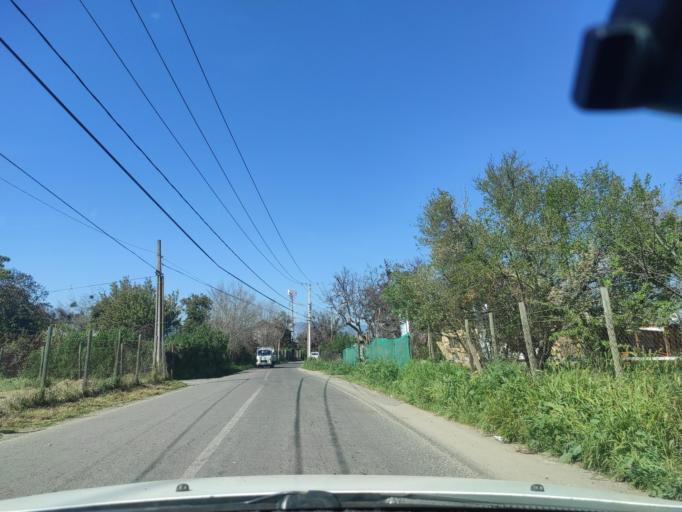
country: CL
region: Valparaiso
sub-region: Provincia de Marga Marga
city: Limache
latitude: -32.9959
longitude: -71.2339
